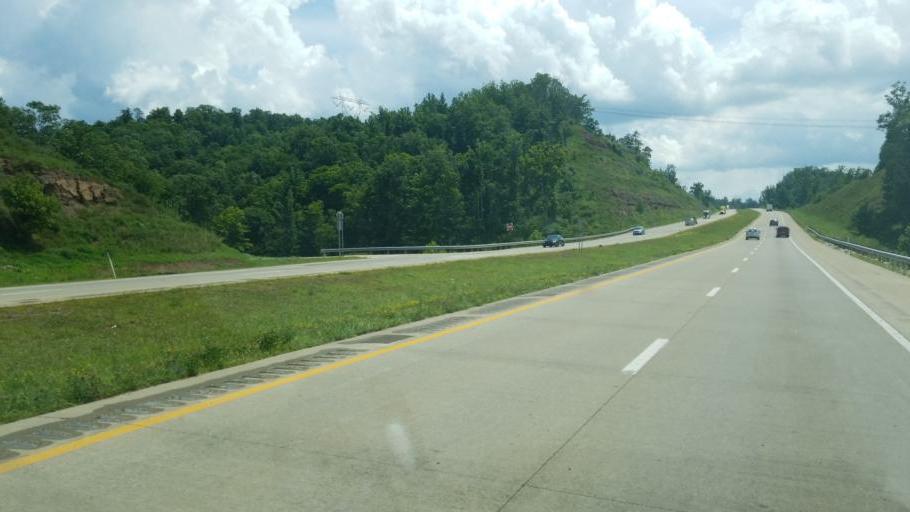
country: US
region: West Virginia
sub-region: Putnam County
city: Eleanor
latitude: 38.5128
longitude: -81.9324
